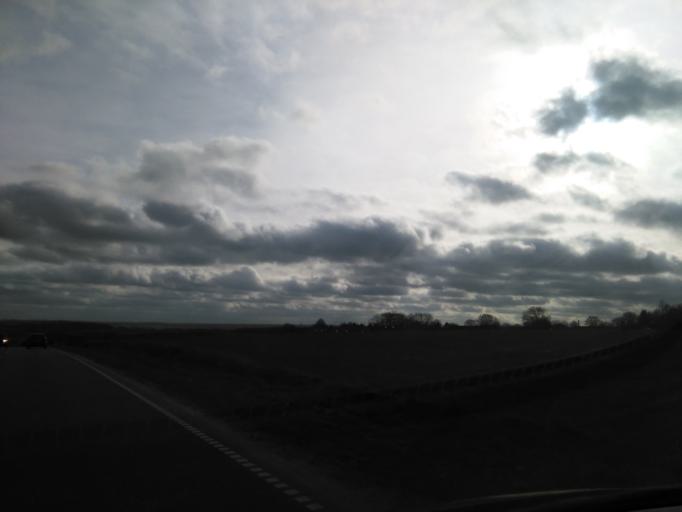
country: DK
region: Central Jutland
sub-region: Arhus Kommune
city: Stavtrup
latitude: 56.1774
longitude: 10.0964
